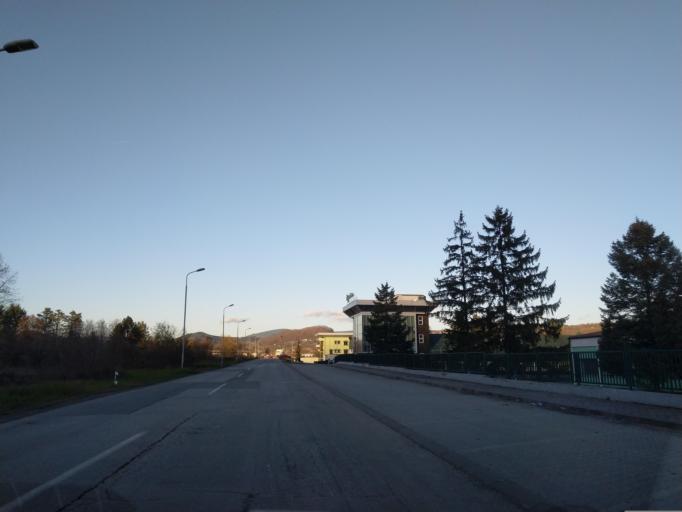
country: RS
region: Central Serbia
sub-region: Zlatiborski Okrug
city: Kosjeric
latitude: 43.9982
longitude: 19.9164
